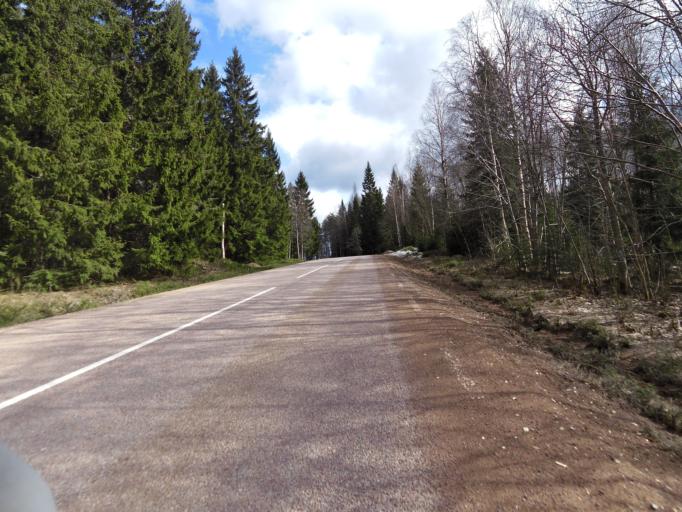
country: SE
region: Dalarna
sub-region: Avesta Kommun
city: Horndal
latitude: 60.2952
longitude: 16.2819
